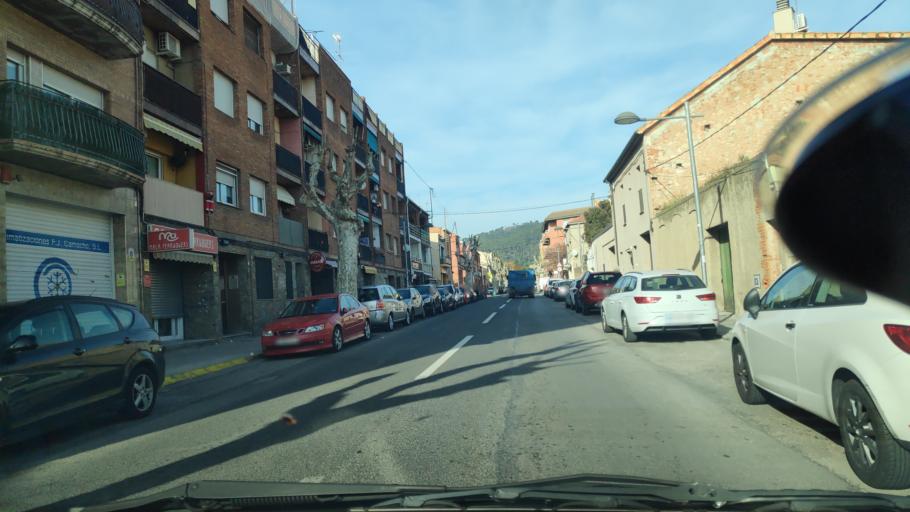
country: ES
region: Catalonia
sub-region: Provincia de Barcelona
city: Castellar del Valles
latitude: 41.6119
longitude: 2.0834
